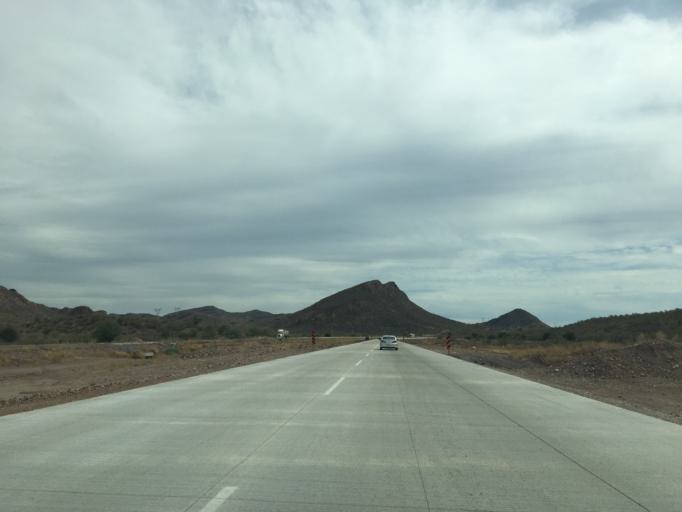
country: MX
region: Sonora
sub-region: Hermosillo
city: Miguel Aleman (La Doce)
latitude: 28.5008
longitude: -111.0448
